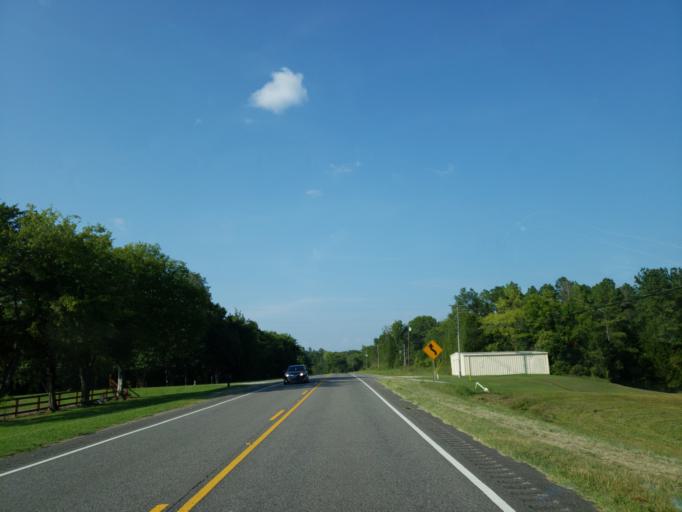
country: US
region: Alabama
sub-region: Sumter County
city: Livingston
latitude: 32.6368
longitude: -88.1736
